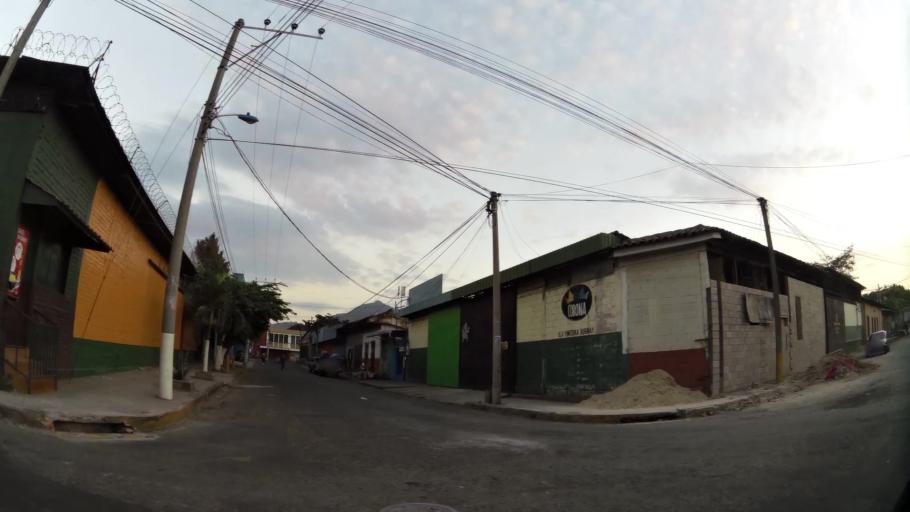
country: SV
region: San Salvador
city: San Salvador
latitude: 13.7042
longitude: -89.1814
